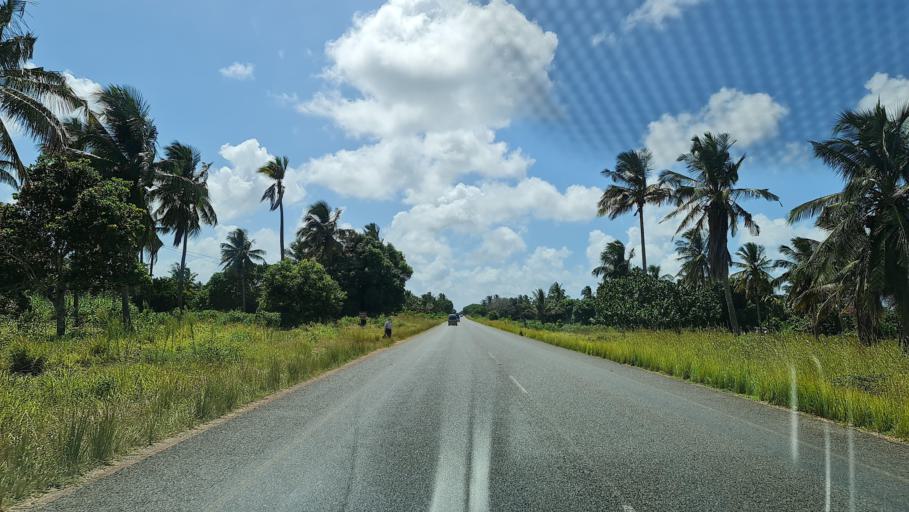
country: MZ
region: Inhambane
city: Maxixe
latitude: -24.5415
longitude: 34.9113
